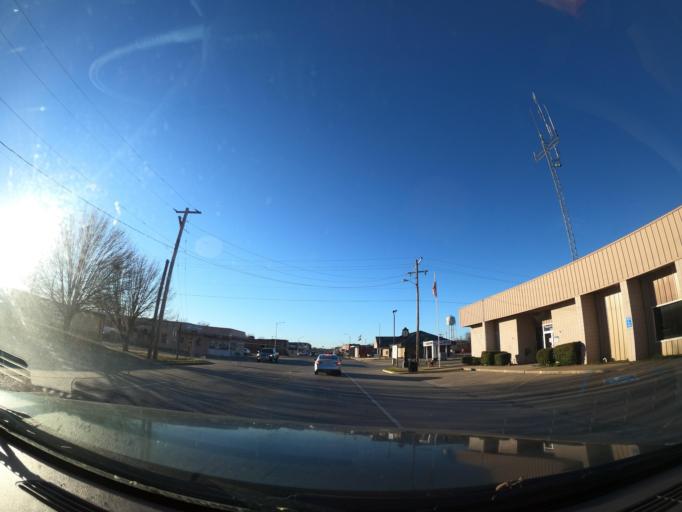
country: US
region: Oklahoma
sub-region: Pittsburg County
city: Hartshorne
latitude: 34.8444
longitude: -95.5541
